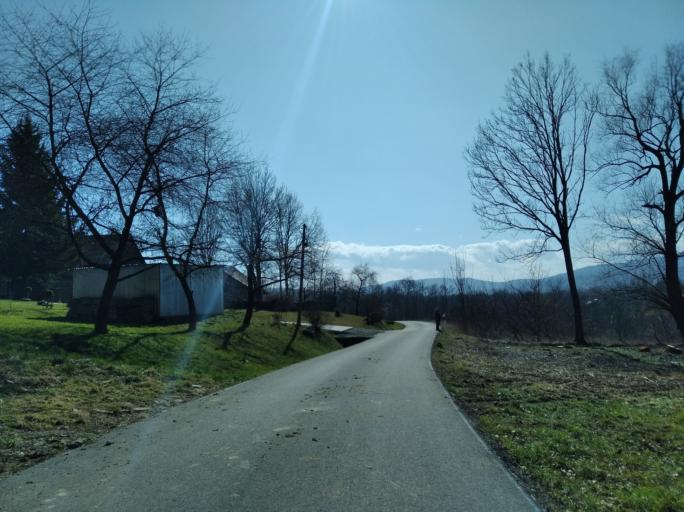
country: PL
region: Subcarpathian Voivodeship
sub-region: Powiat strzyzowski
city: Wysoka Strzyzowska
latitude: 49.8361
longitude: 21.7443
